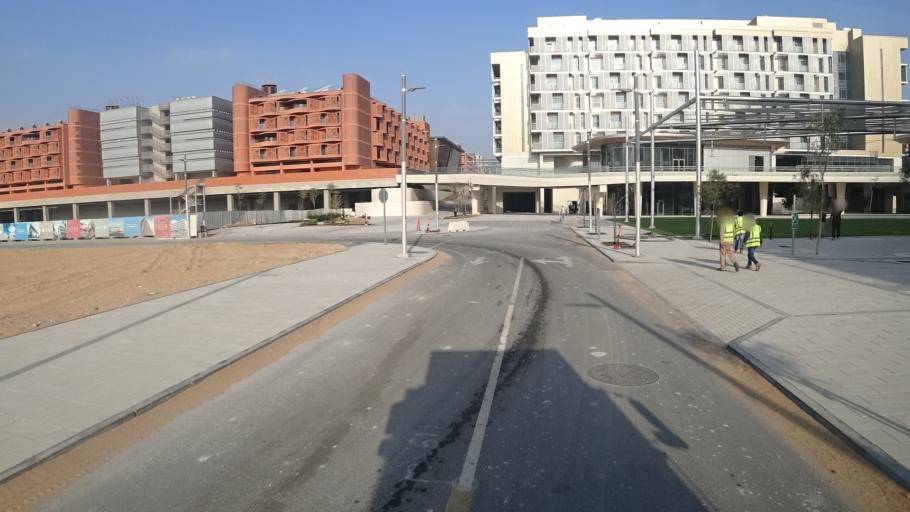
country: AE
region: Abu Dhabi
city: Abu Dhabi
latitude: 24.4327
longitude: 54.6206
